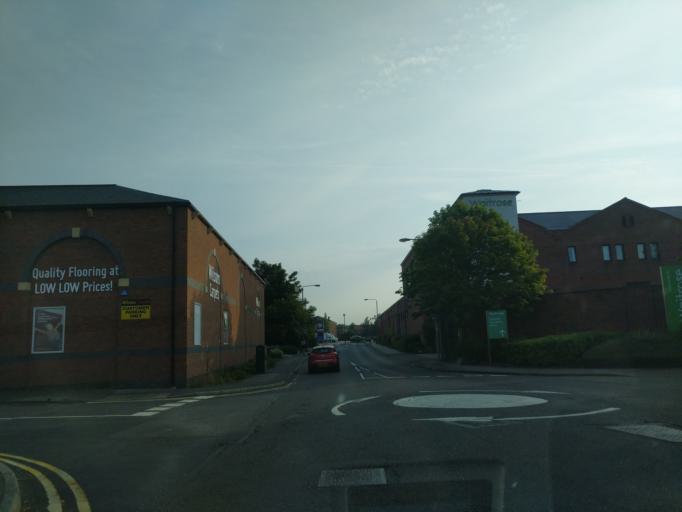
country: GB
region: England
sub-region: Nottinghamshire
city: Newark on Trent
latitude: 53.0793
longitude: -0.8130
